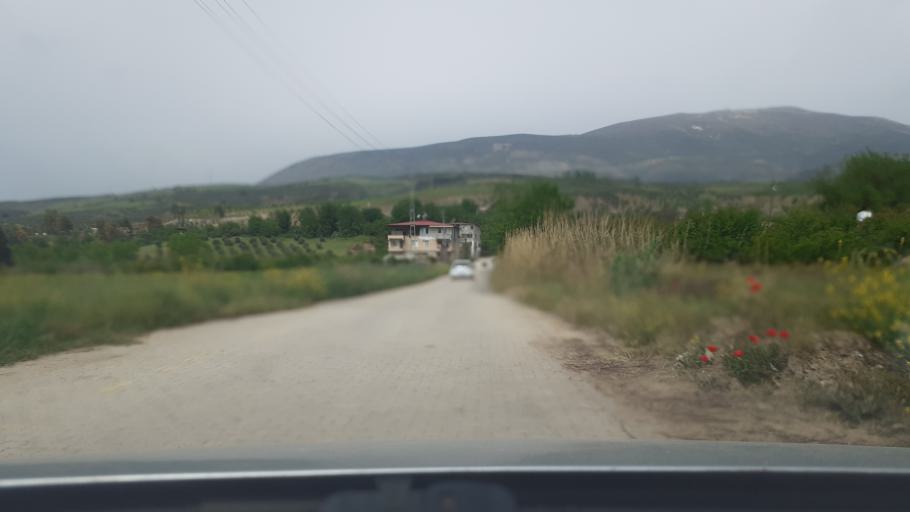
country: TR
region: Hatay
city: Kirikhan
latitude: 36.4743
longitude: 36.3192
